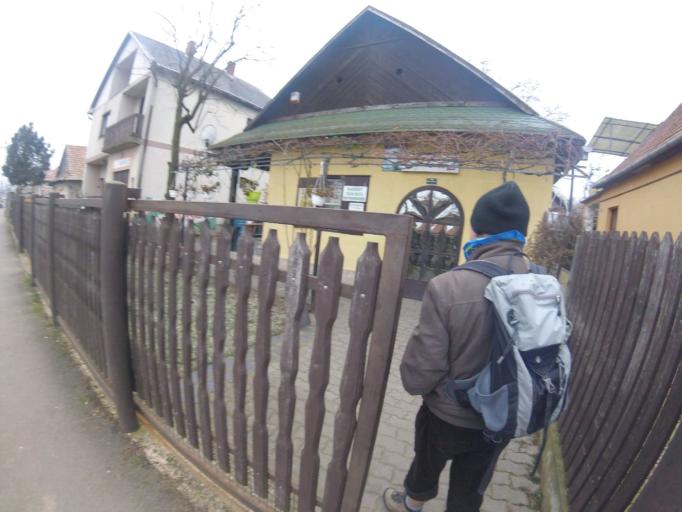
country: HU
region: Nograd
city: Paszto
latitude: 47.9491
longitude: 19.6958
